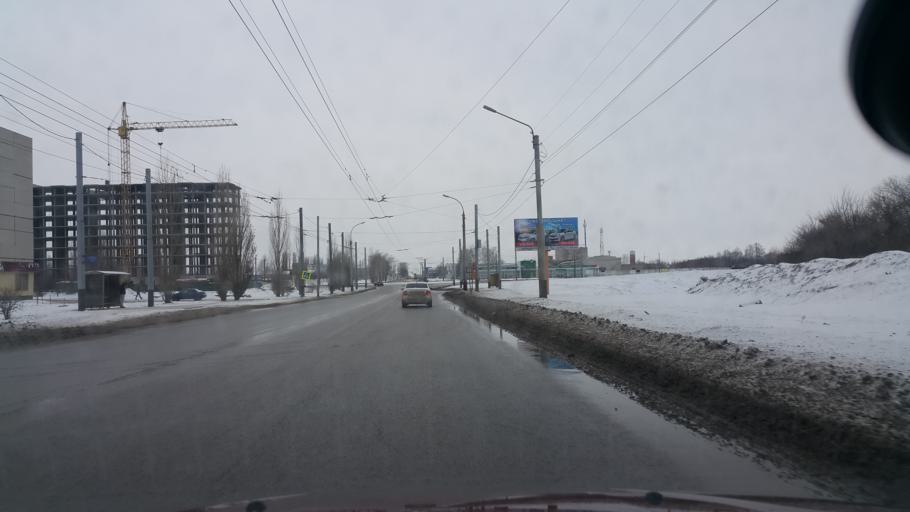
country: RU
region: Tambov
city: Tambov
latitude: 52.7379
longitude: 41.3804
